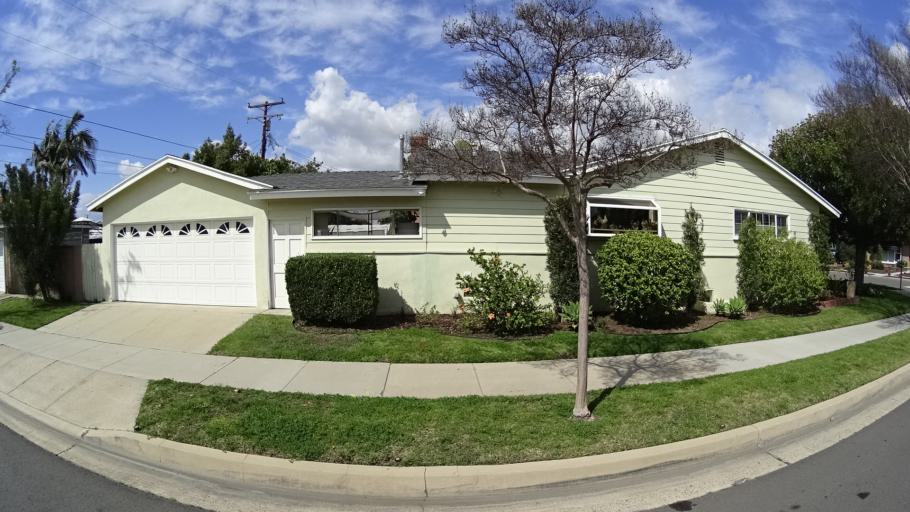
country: US
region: California
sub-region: Orange County
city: Anaheim
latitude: 33.8381
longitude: -117.9231
